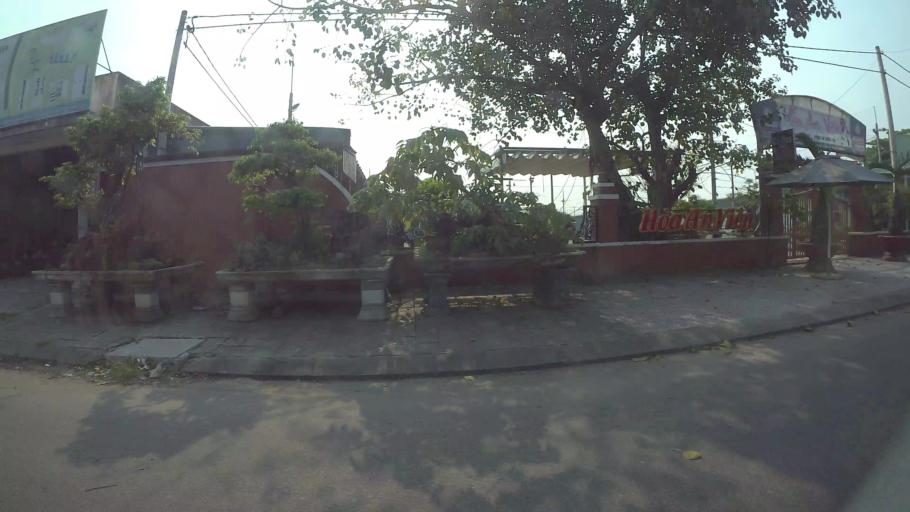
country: VN
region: Da Nang
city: Thanh Khe
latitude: 16.0539
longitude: 108.1746
